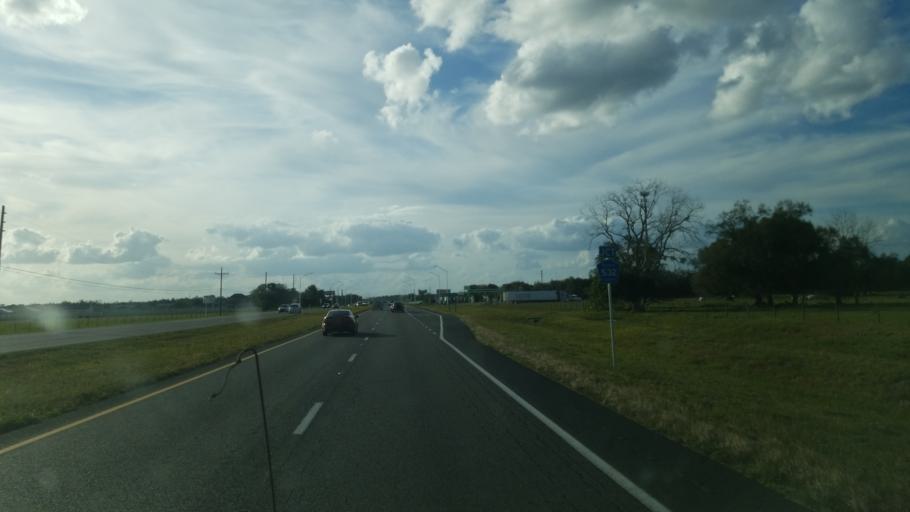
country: US
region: Florida
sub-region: Osceola County
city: Saint Cloud
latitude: 28.2434
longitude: -81.2205
